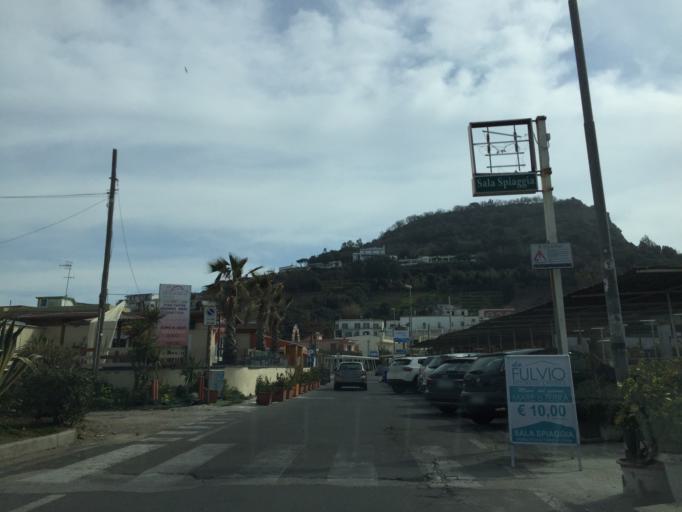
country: IT
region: Campania
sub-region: Provincia di Napoli
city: Bacoli
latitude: 40.7864
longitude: 14.0834
